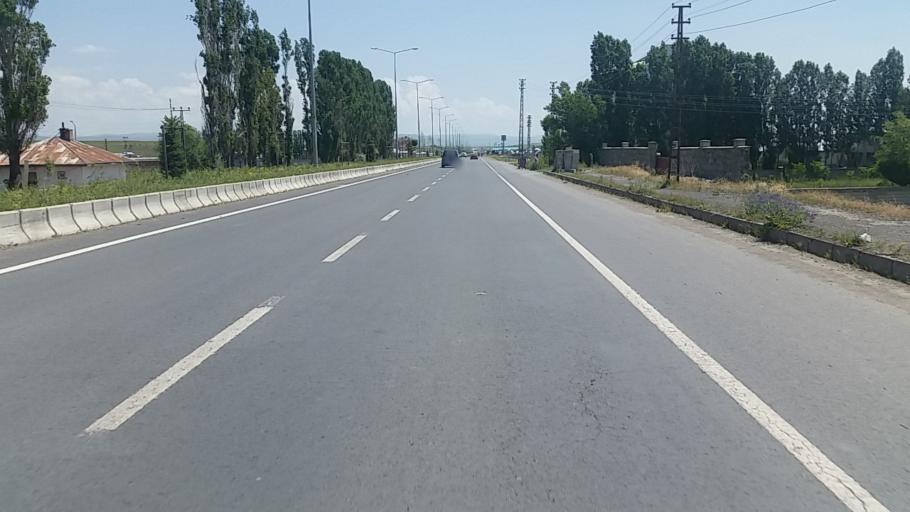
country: TR
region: Agri
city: Agri
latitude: 39.7122
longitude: 43.0848
